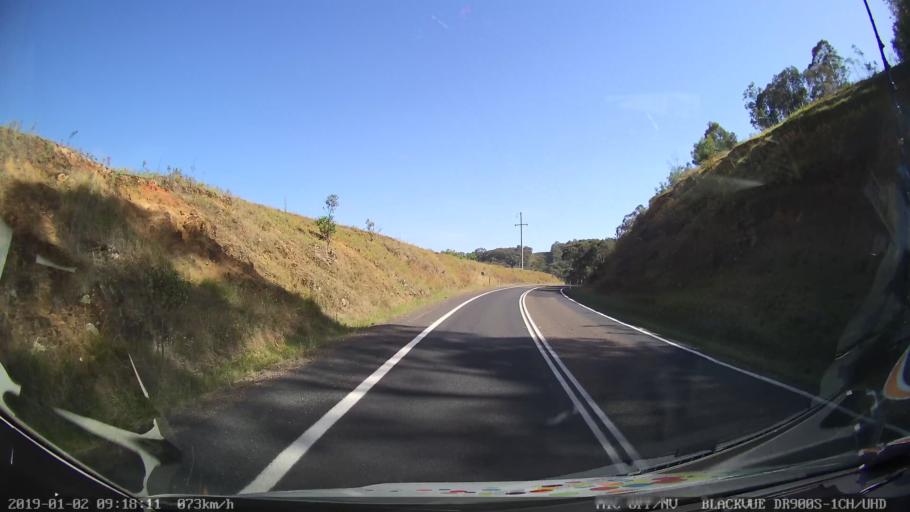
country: AU
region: New South Wales
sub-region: Tumut Shire
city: Tumut
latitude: -35.4317
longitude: 148.2853
